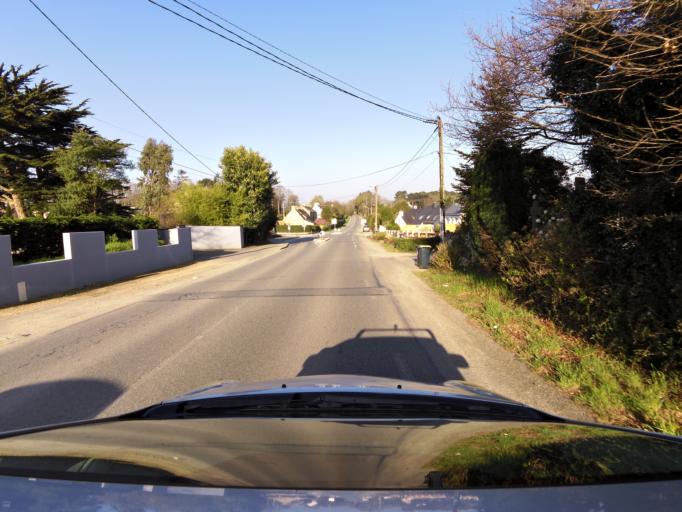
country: FR
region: Brittany
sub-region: Departement du Morbihan
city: Ploemeur
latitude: 47.7384
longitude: -3.4434
